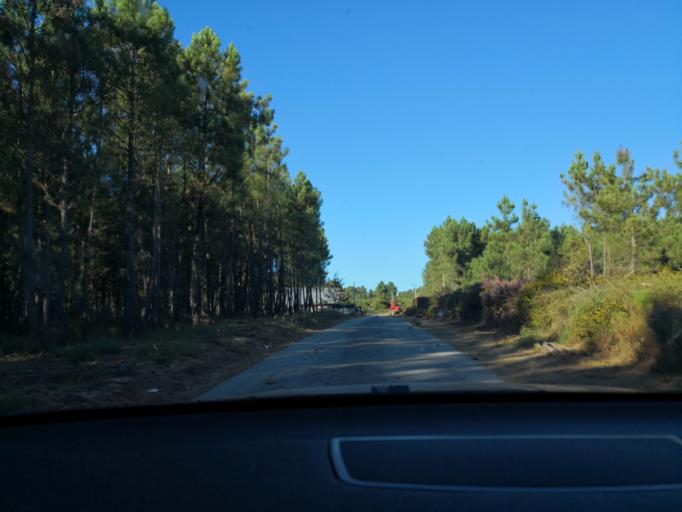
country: PT
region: Vila Real
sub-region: Sabrosa
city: Vilela
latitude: 41.2529
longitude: -7.6256
